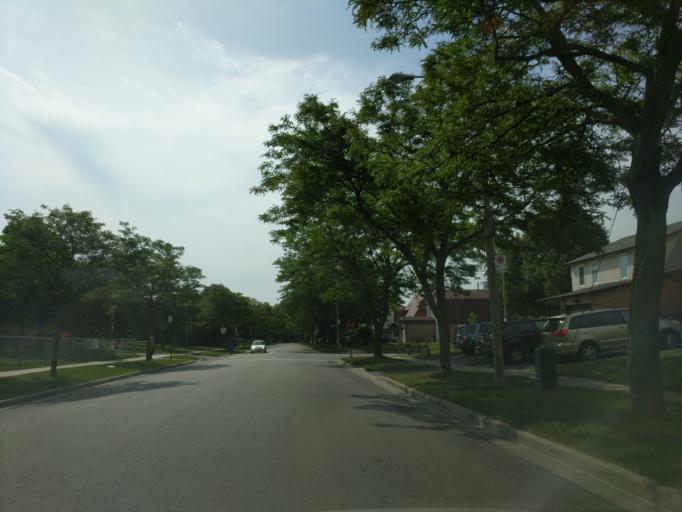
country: CA
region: Ontario
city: Scarborough
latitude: 43.8083
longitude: -79.2862
